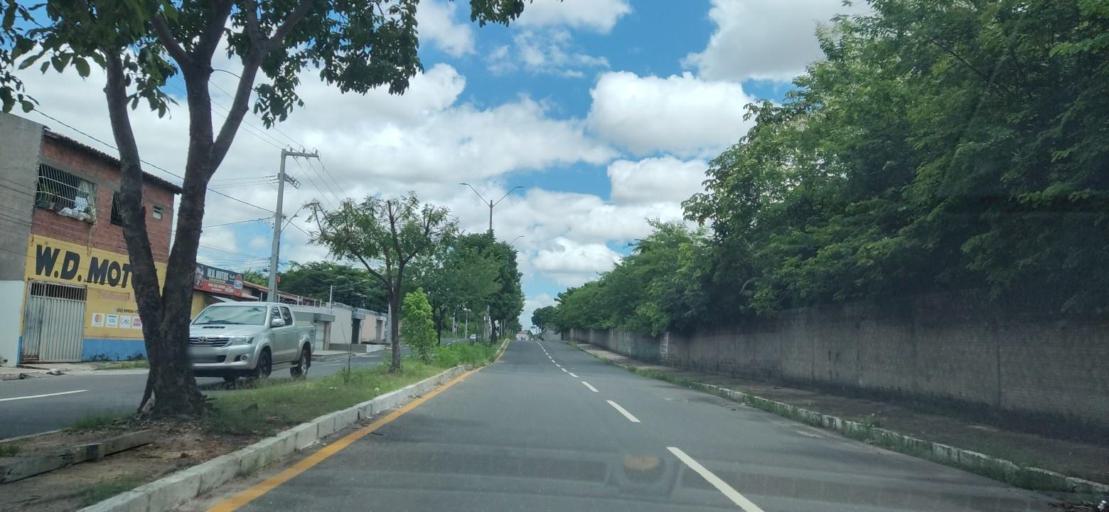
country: BR
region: Piaui
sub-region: Teresina
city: Teresina
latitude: -5.0646
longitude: -42.7557
